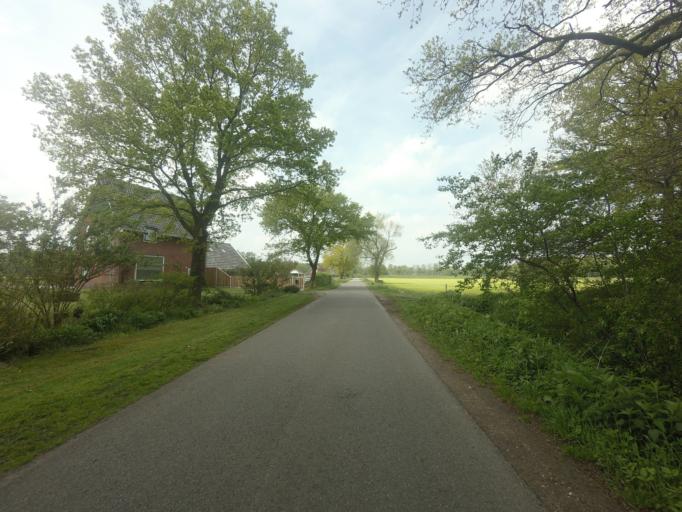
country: NL
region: Overijssel
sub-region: Gemeente Hof van Twente
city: Delden
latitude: 52.2483
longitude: 6.6912
